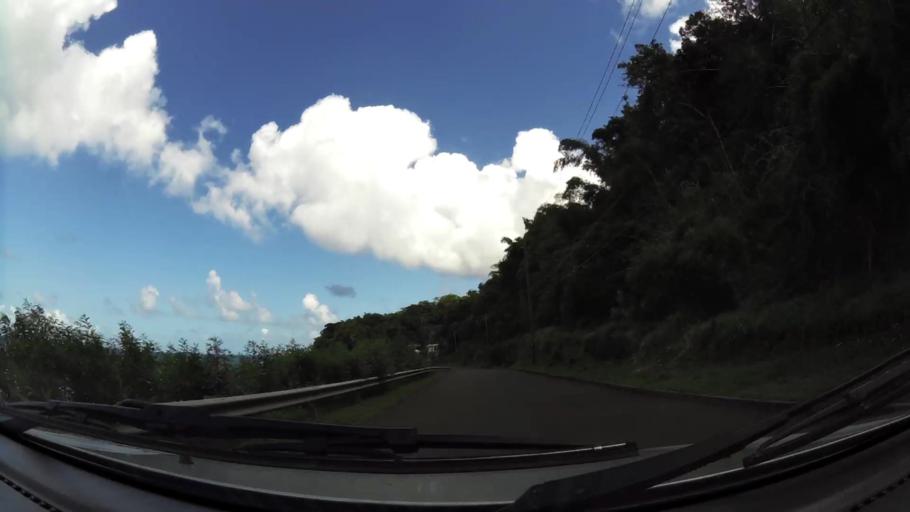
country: GD
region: Saint Mark
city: Victoria
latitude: 12.1863
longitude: -61.7200
